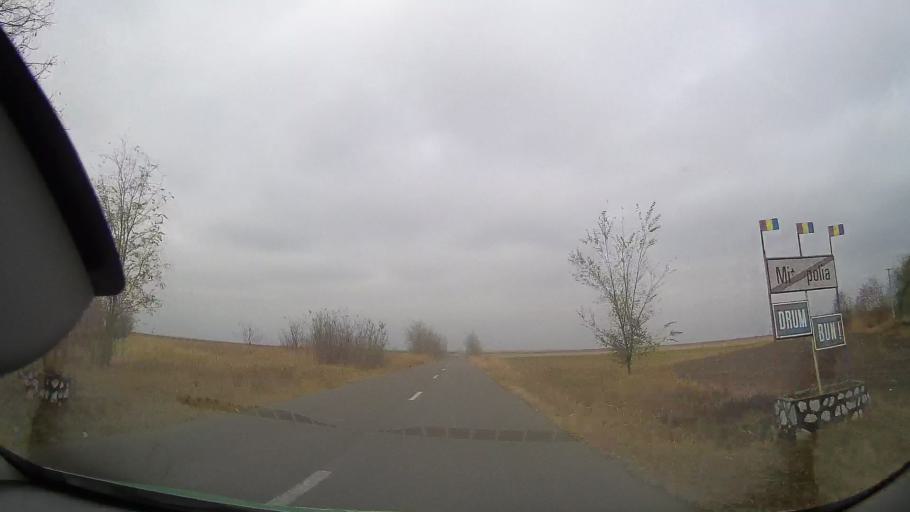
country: RO
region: Buzau
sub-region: Comuna Scutelnici
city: Scutelnici
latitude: 44.8828
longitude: 26.8762
